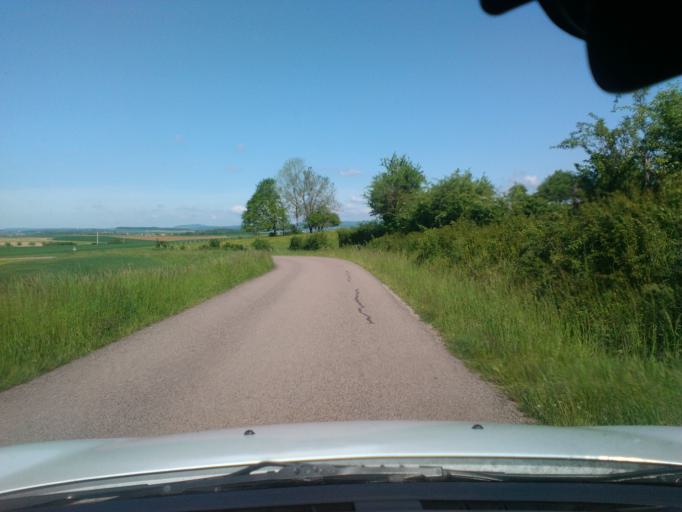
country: FR
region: Lorraine
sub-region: Departement des Vosges
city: Mirecourt
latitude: 48.3087
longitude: 6.1701
